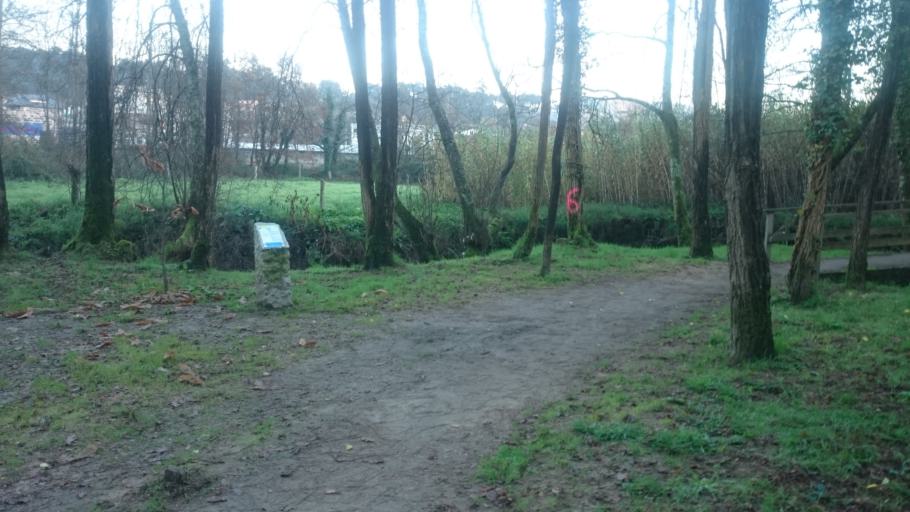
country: ES
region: Galicia
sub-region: Provincia de Pontevedra
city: Porrino
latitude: 42.1524
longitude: -8.6238
